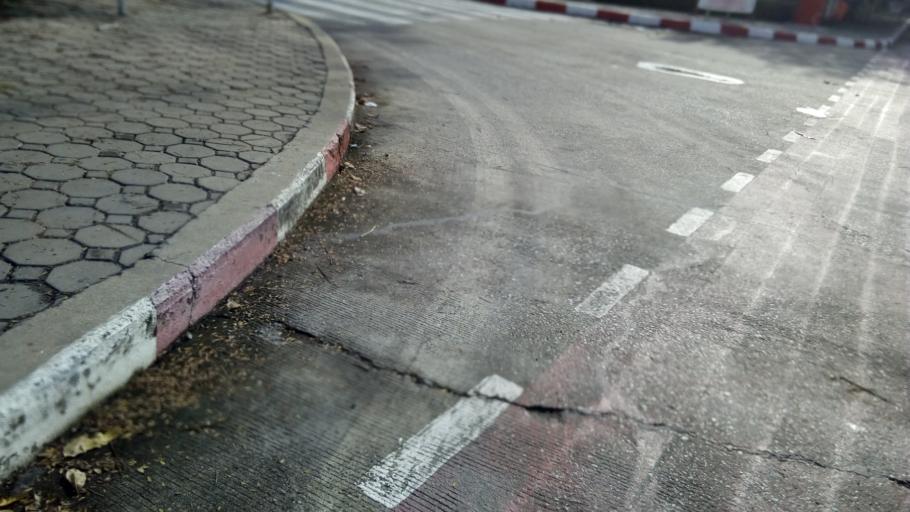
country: TH
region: Nakhon Nayok
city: Ongkharak
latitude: 14.1060
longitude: 100.9867
